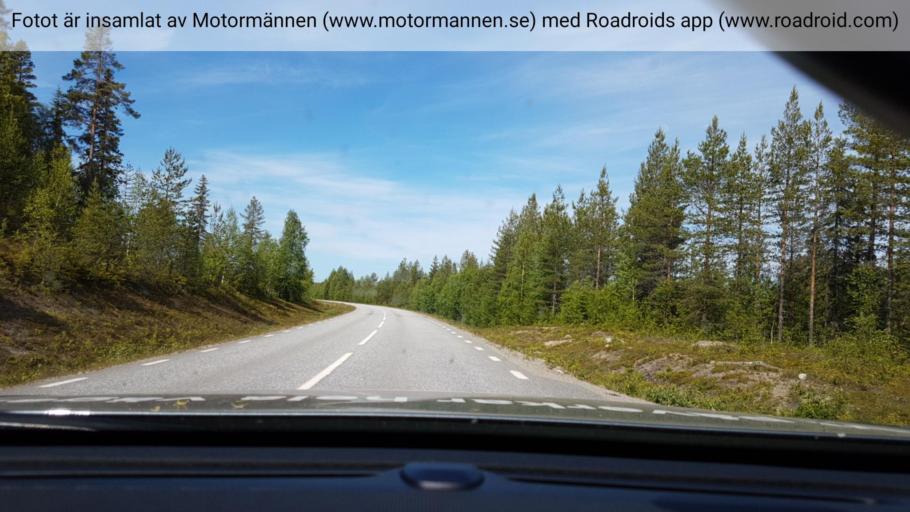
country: SE
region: Vaesterbotten
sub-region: Dorotea Kommun
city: Dorotea
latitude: 64.2385
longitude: 16.7839
